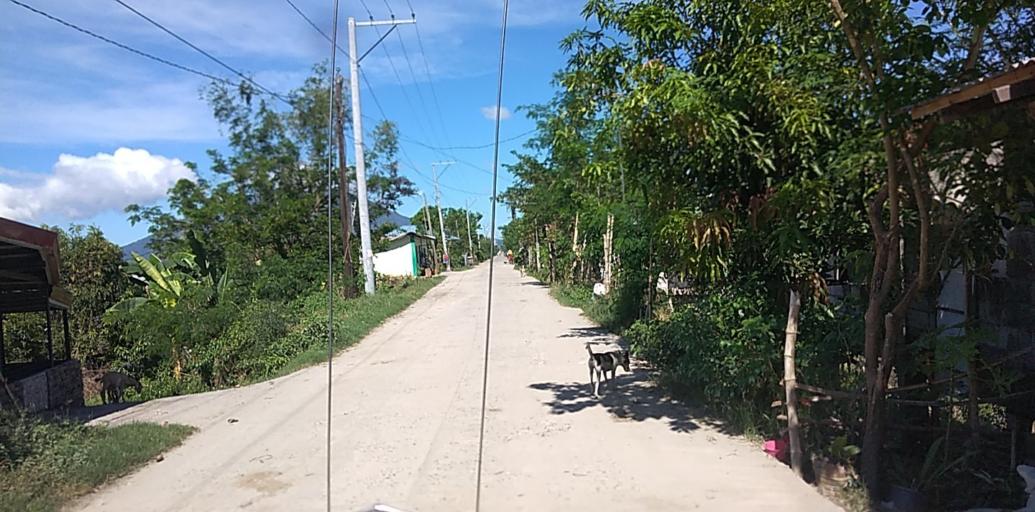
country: PH
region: Central Luzon
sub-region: Province of Pampanga
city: Candating
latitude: 15.1247
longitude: 120.8115
